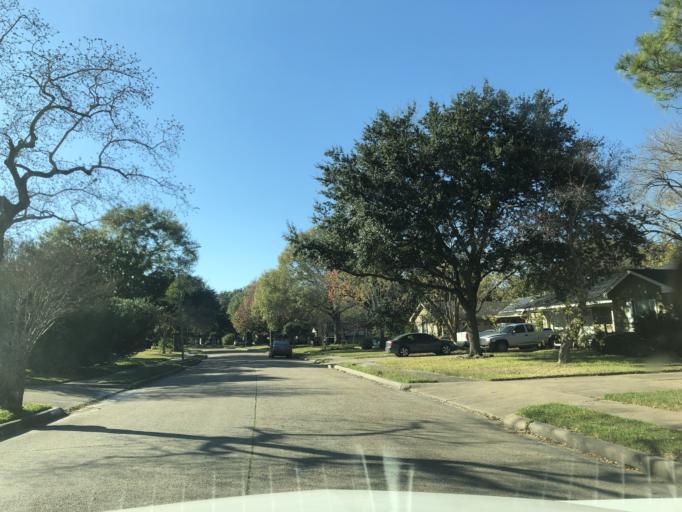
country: US
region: Texas
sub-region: Harris County
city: Bellaire
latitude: 29.6965
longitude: -95.5078
